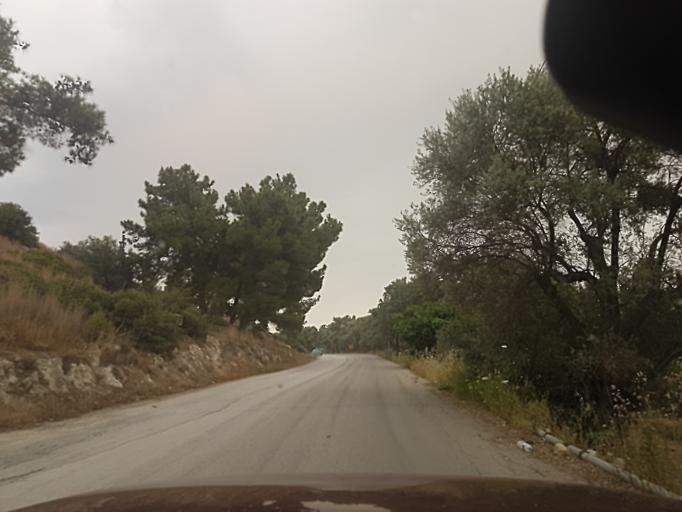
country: GR
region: Central Greece
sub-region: Nomos Evvoias
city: Filla
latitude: 38.4435
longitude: 23.6691
